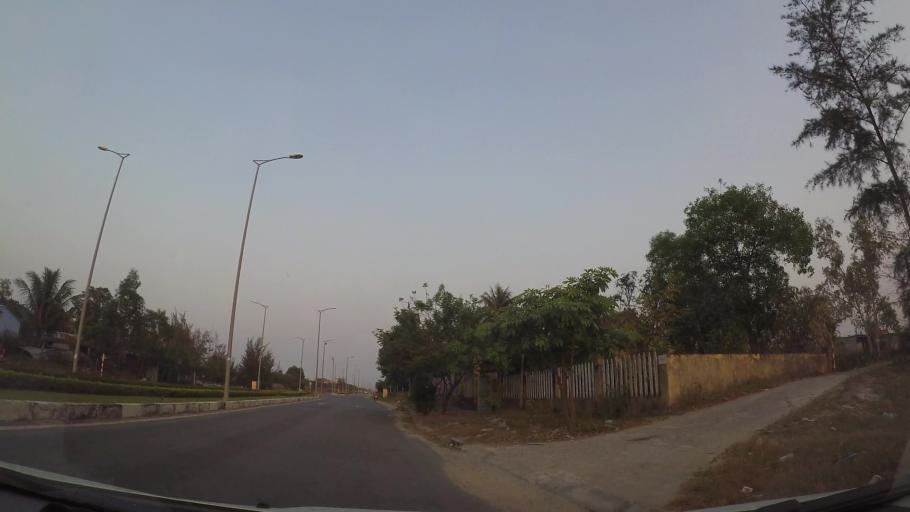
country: VN
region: Da Nang
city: Ngu Hanh Son
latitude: 15.9778
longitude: 108.2393
